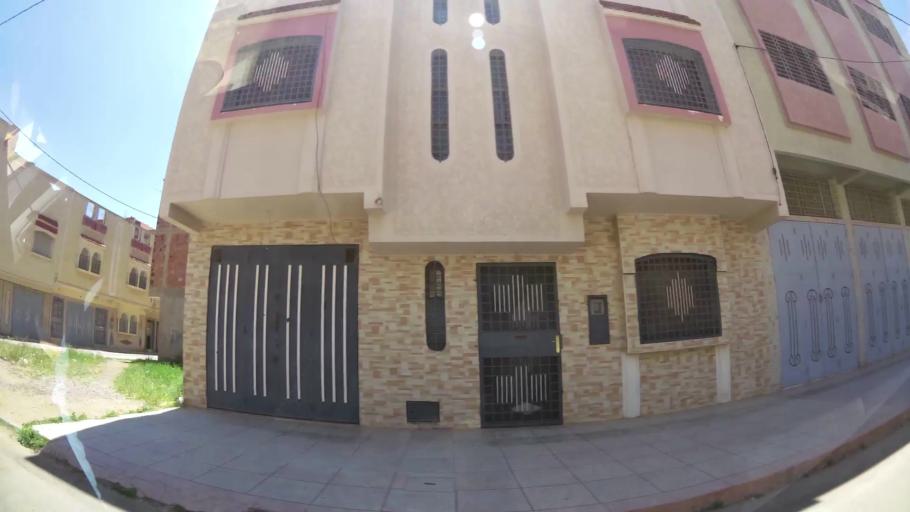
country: MA
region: Oriental
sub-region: Oujda-Angad
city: Oujda
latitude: 34.6652
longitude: -1.9366
